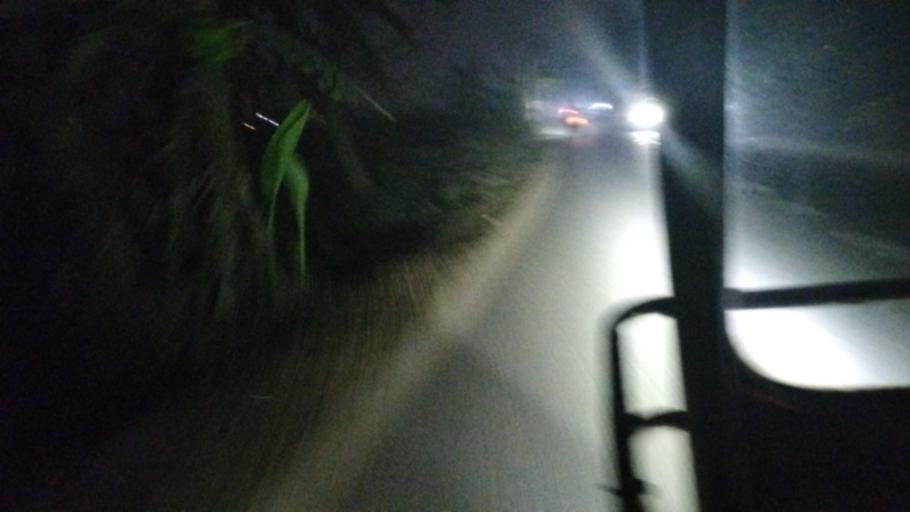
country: BD
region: Dhaka
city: Gafargaon
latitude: 24.3999
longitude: 90.3708
